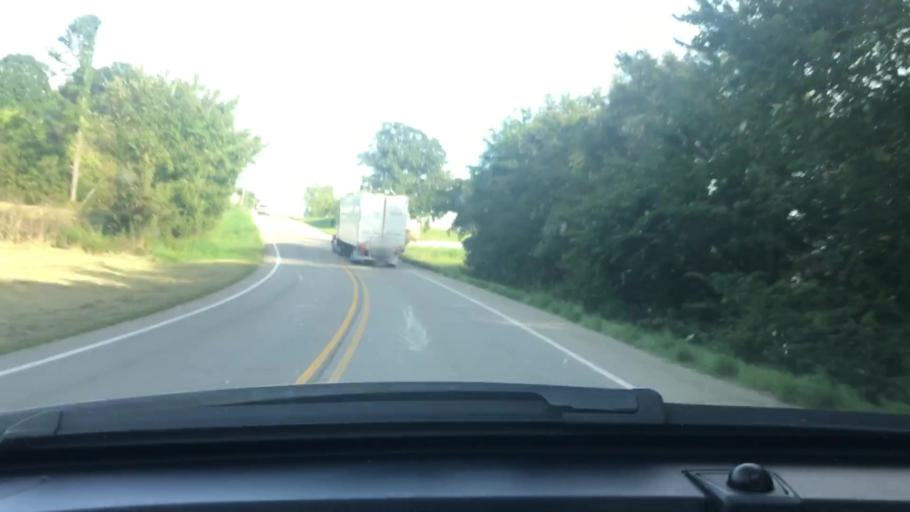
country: US
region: Arkansas
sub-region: Sharp County
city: Cherokee Village
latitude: 36.2400
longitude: -91.2640
